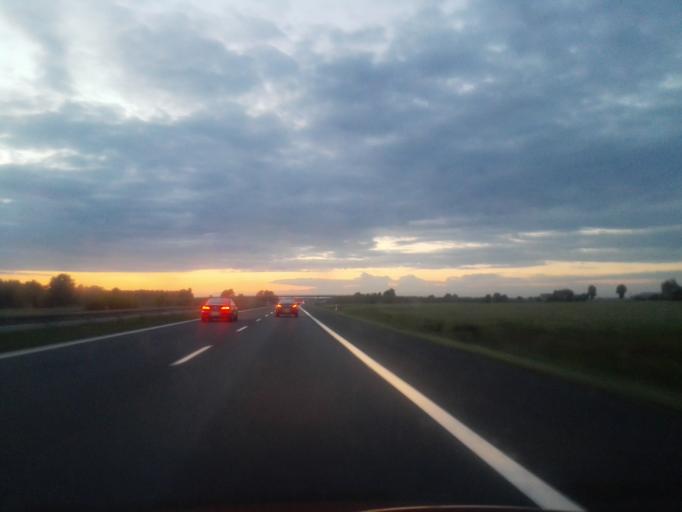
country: PL
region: Lodz Voivodeship
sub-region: Powiat piotrkowski
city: Grabica
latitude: 51.5050
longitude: 19.6044
